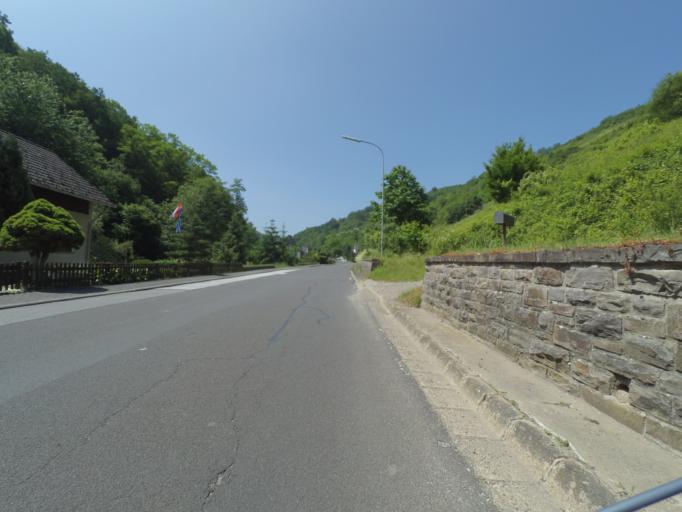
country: DE
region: Rheinland-Pfalz
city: Sankt Goar
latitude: 50.1511
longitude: 7.6980
